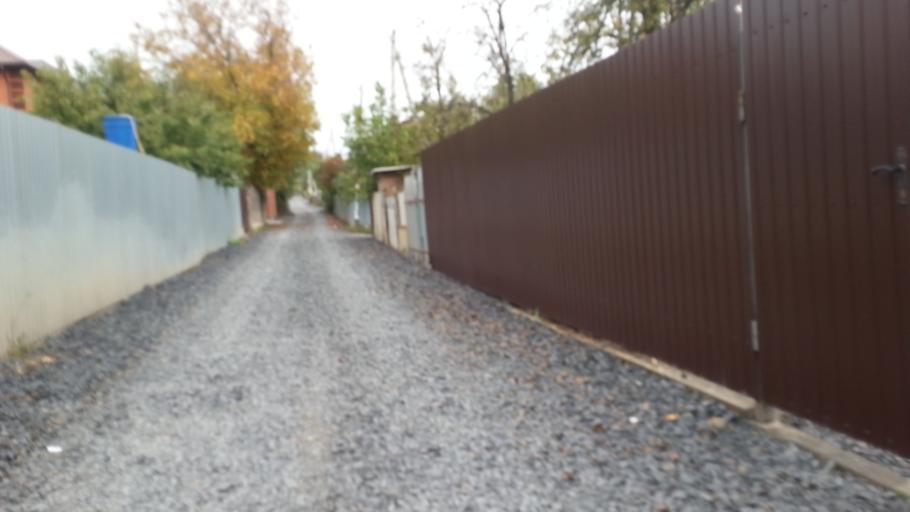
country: RU
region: Rostov
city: Severnyy
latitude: 47.2936
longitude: 39.6674
